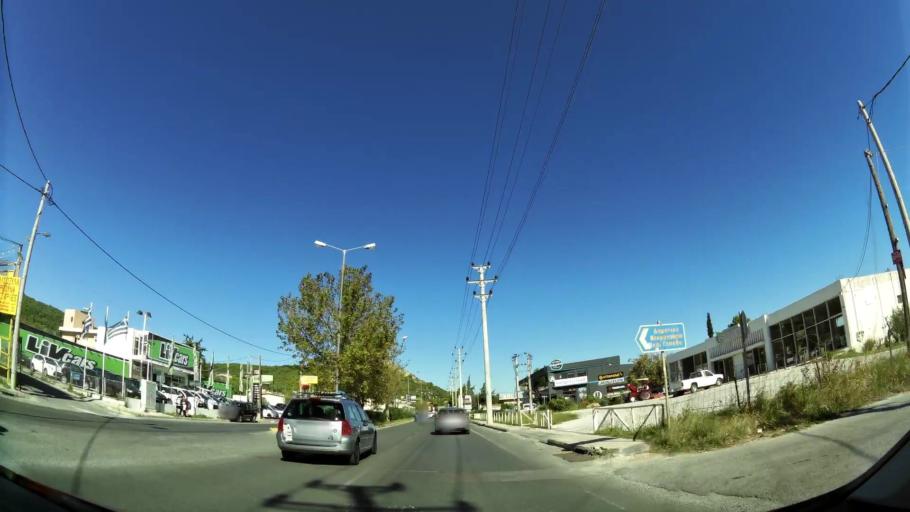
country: GR
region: Attica
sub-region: Nomarchia Anatolikis Attikis
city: Leondarion
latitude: 37.9950
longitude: 23.8479
